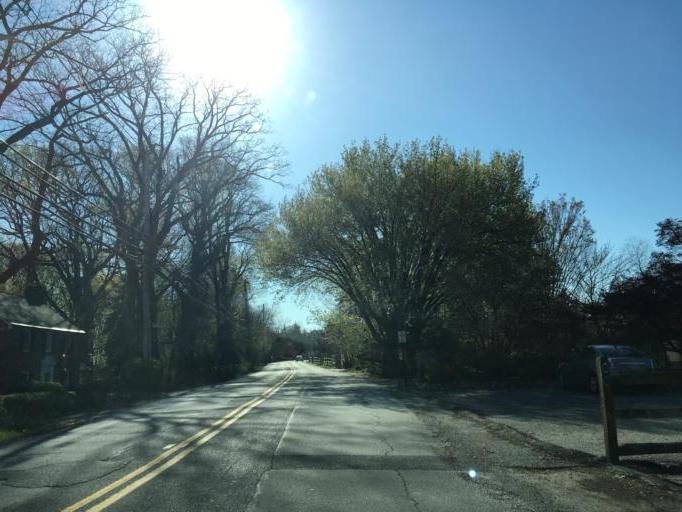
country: US
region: Maryland
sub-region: Baltimore County
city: Towson
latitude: 39.4063
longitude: -76.6142
